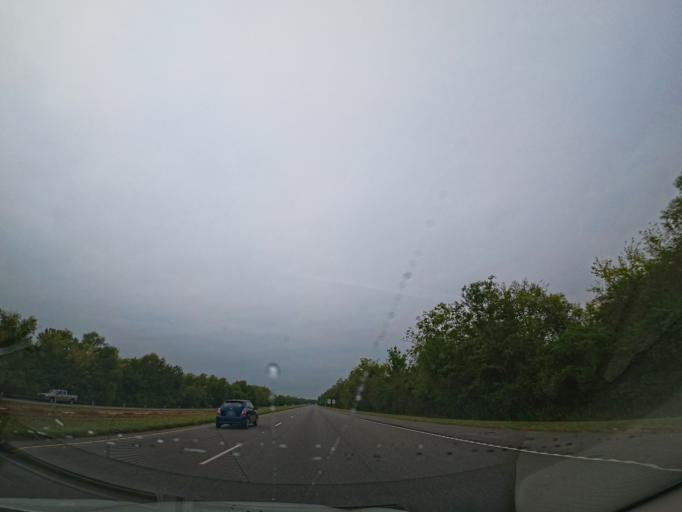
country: US
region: Louisiana
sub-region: Lafourche Parish
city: Raceland
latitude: 29.7021
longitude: -90.5776
